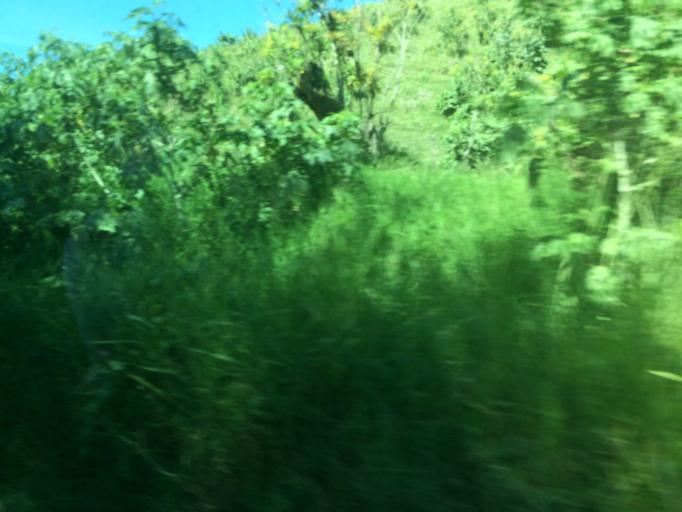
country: MX
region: Colima
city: Suchitlan
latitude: 19.4254
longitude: -103.6932
